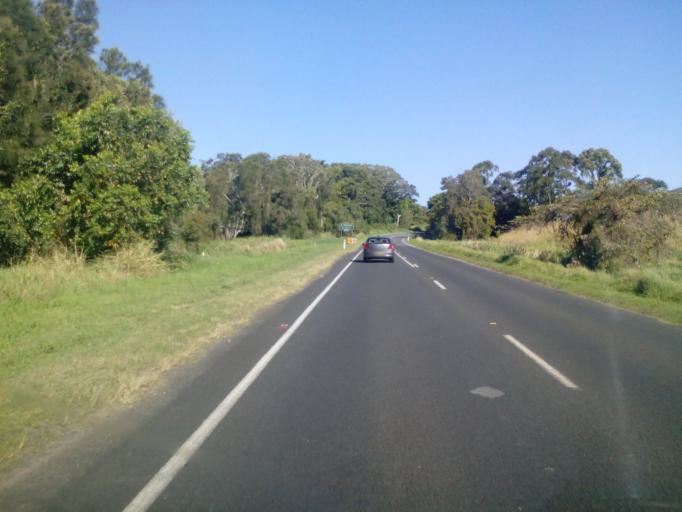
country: AU
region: New South Wales
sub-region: Tweed
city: Kingscliff
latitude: -28.2597
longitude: 153.5609
